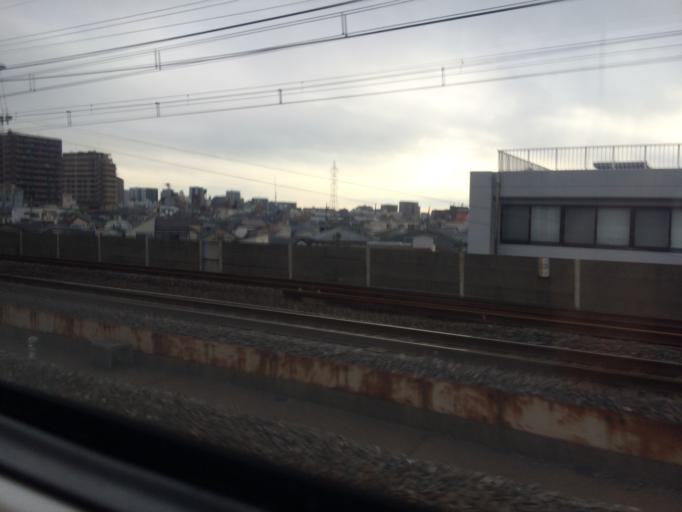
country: JP
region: Tokyo
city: Urayasu
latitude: 35.7142
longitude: 139.8536
